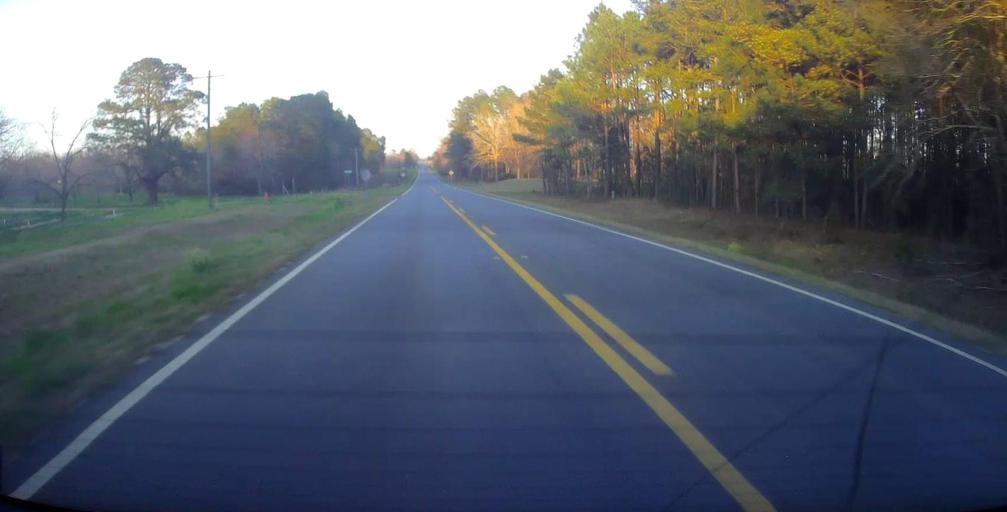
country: US
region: Georgia
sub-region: Dodge County
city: Chester
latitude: 32.3507
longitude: -83.0306
